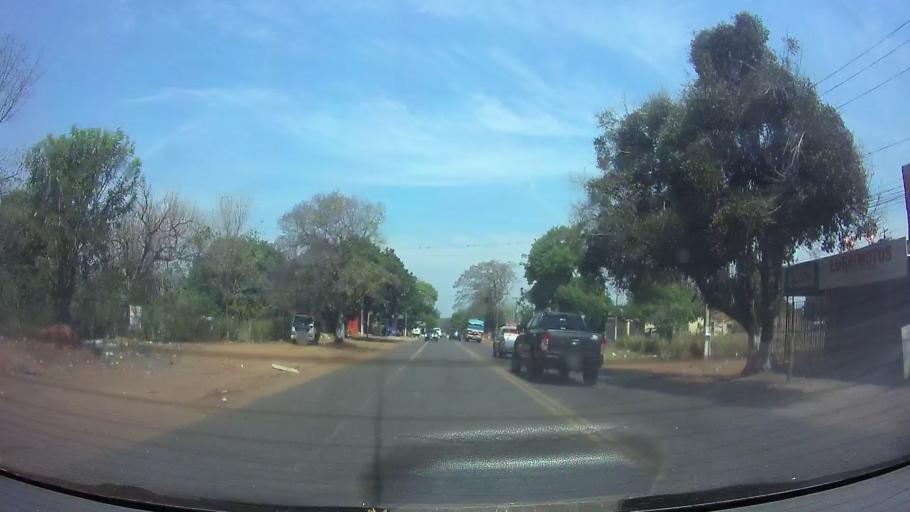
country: PY
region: Central
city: Capiata
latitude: -25.4087
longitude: -57.4605
